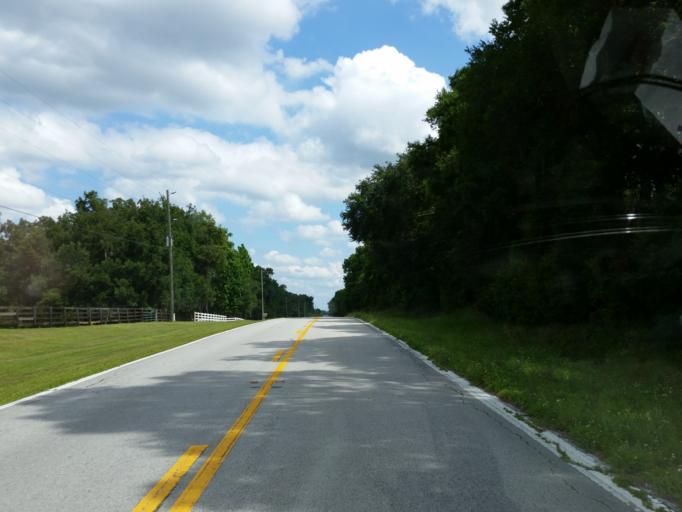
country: US
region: Florida
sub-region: Citrus County
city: Floral City
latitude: 28.6745
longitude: -82.3600
